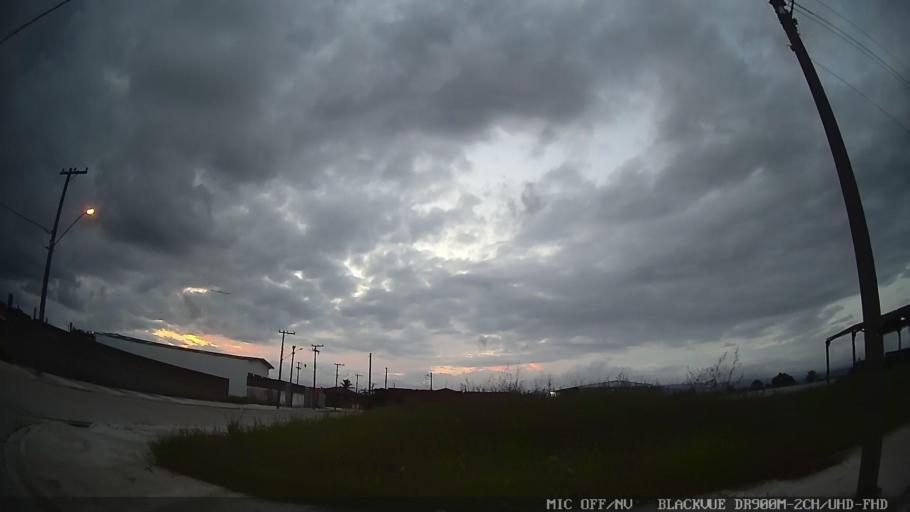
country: BR
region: Sao Paulo
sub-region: Itanhaem
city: Itanhaem
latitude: -24.1898
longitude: -46.8312
